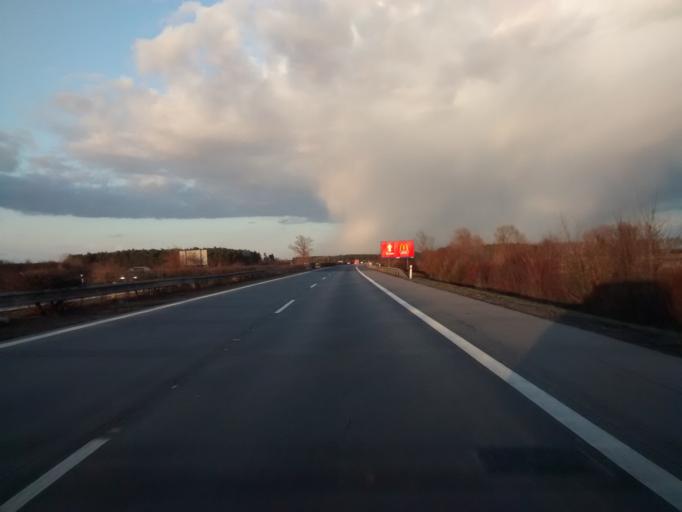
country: CZ
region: Central Bohemia
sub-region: Okres Nymburk
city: Sadska
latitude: 50.1209
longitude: 14.9975
